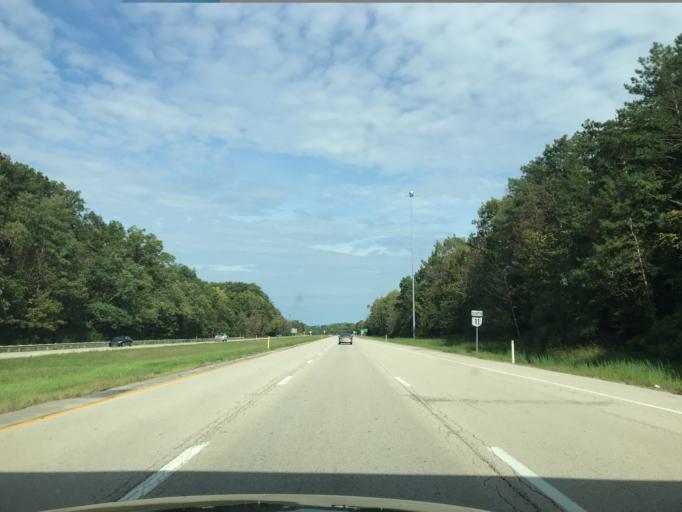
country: US
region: Ohio
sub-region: Ashtabula County
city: Ashtabula
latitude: 41.8331
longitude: -80.7655
